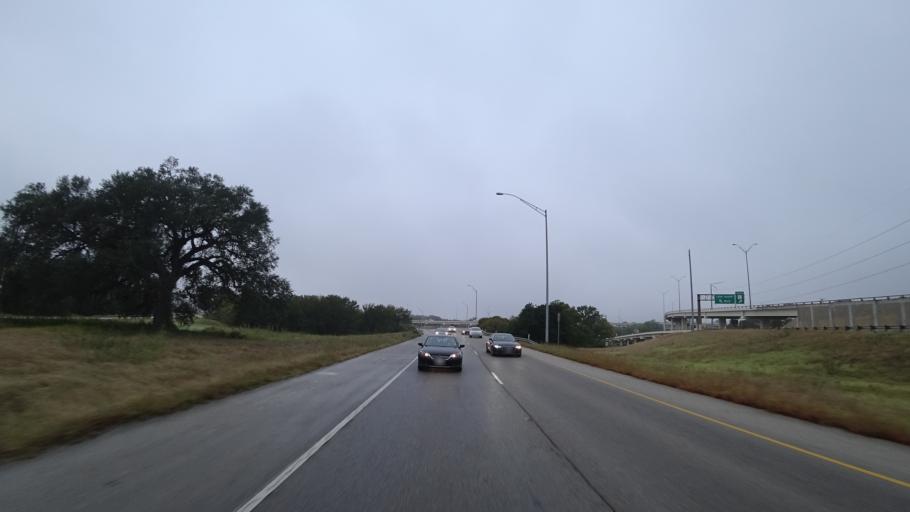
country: US
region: Texas
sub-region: Travis County
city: Rollingwood
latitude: 30.2749
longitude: -97.7670
